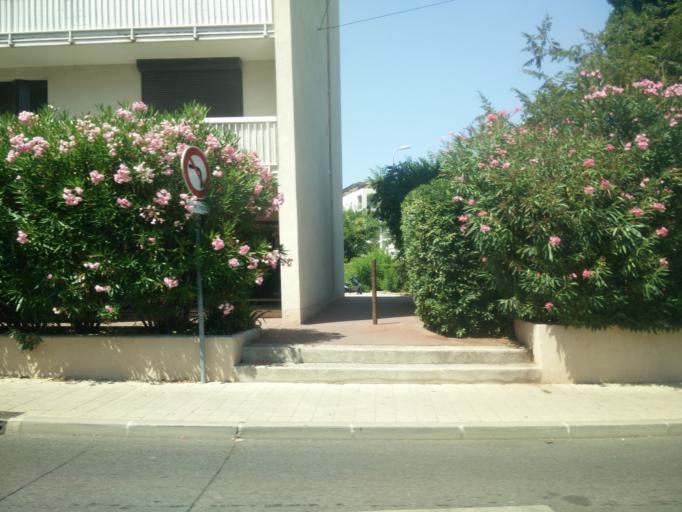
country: FR
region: Languedoc-Roussillon
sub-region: Departement de l'Herault
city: Montpellier
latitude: 43.6039
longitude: 3.8927
